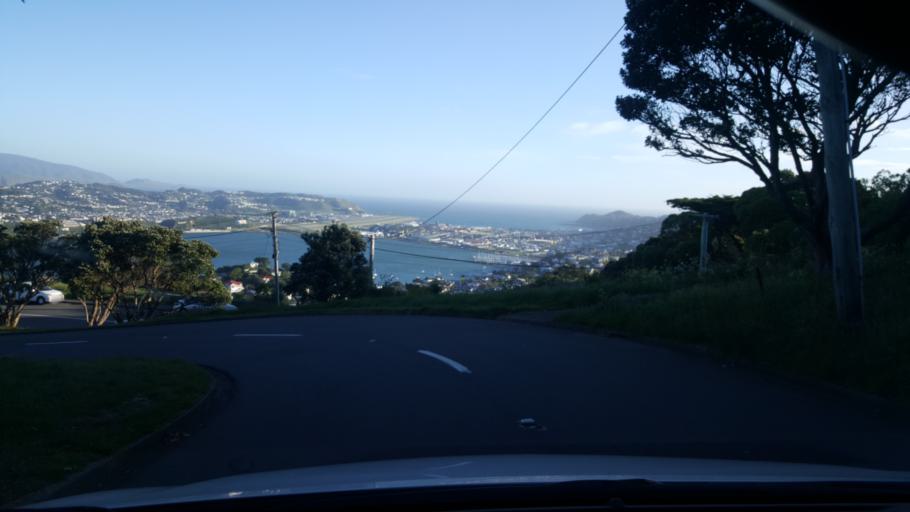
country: NZ
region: Wellington
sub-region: Wellington City
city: Wellington
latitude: -41.2953
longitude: 174.7984
